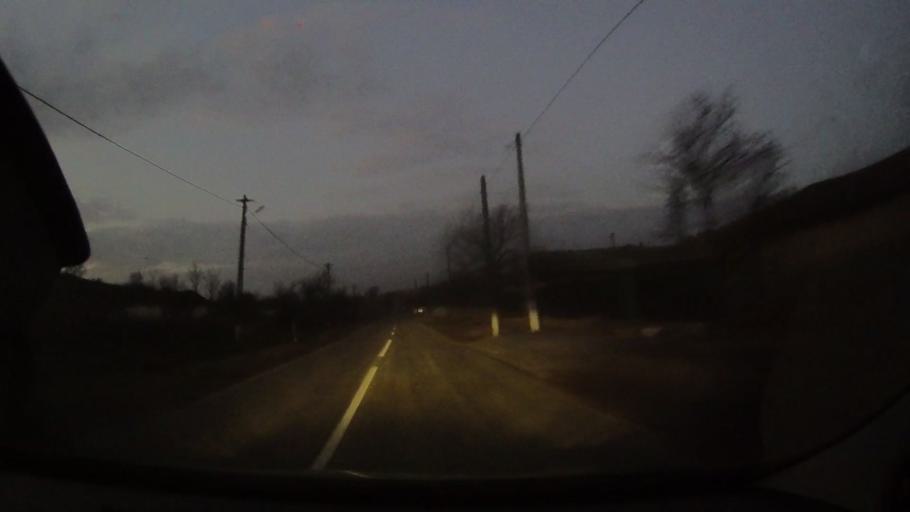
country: RO
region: Constanta
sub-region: Comuna Aliman
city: Aliman
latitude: 44.1441
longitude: 27.8333
